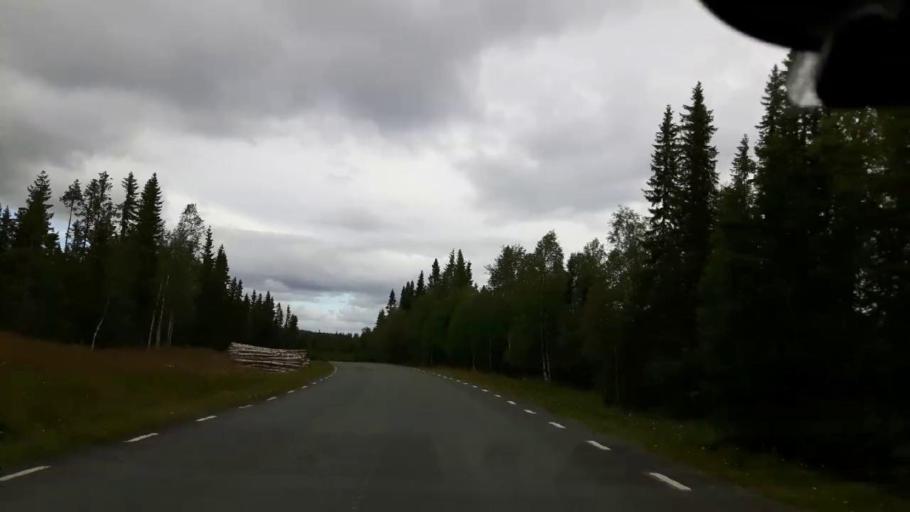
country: SE
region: Jaemtland
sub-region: Krokoms Kommun
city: Valla
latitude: 63.5463
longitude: 13.8524
